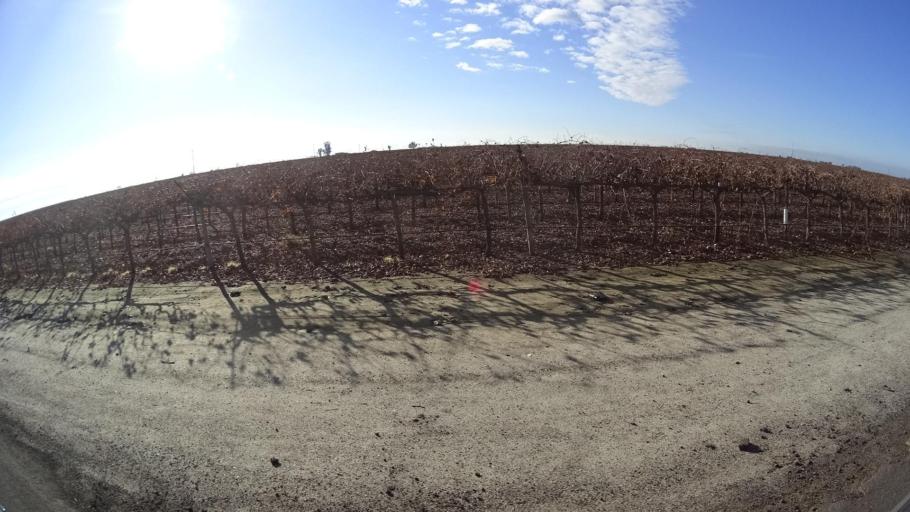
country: US
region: California
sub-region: Kern County
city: Delano
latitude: 35.7322
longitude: -119.2953
